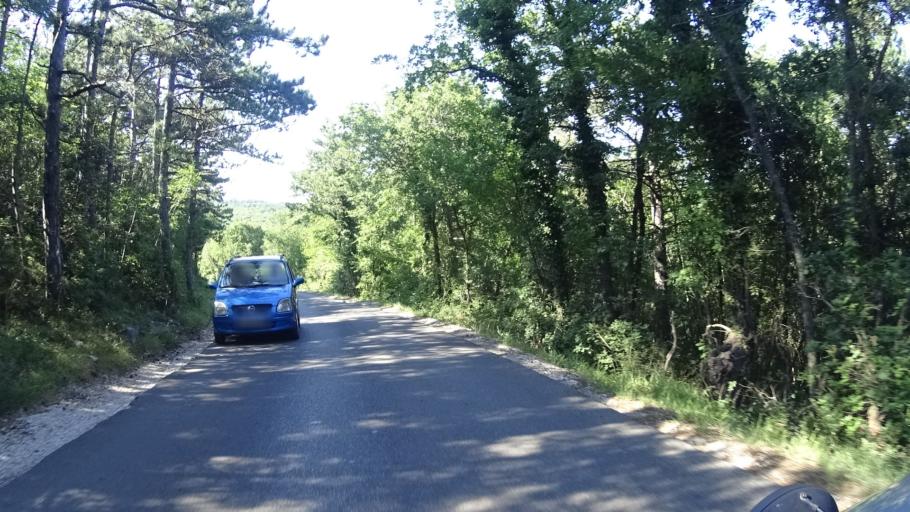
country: HR
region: Istarska
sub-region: Grad Labin
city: Labin
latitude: 45.0641
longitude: 14.1257
